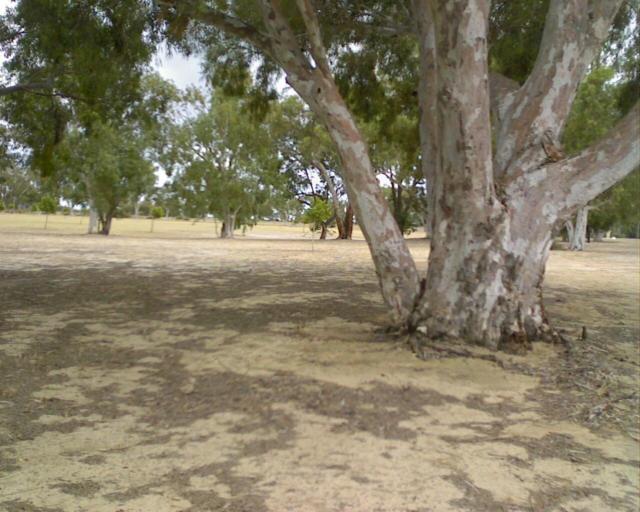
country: AU
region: Western Australia
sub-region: Dandaragan
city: Jurien Bay
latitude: -29.8242
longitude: 115.2654
